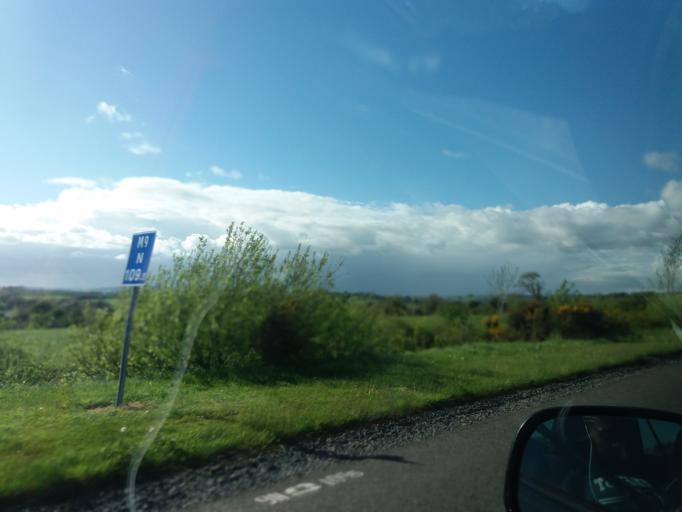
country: IE
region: Leinster
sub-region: Kilkenny
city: Mooncoin
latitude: 52.3611
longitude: -7.1654
